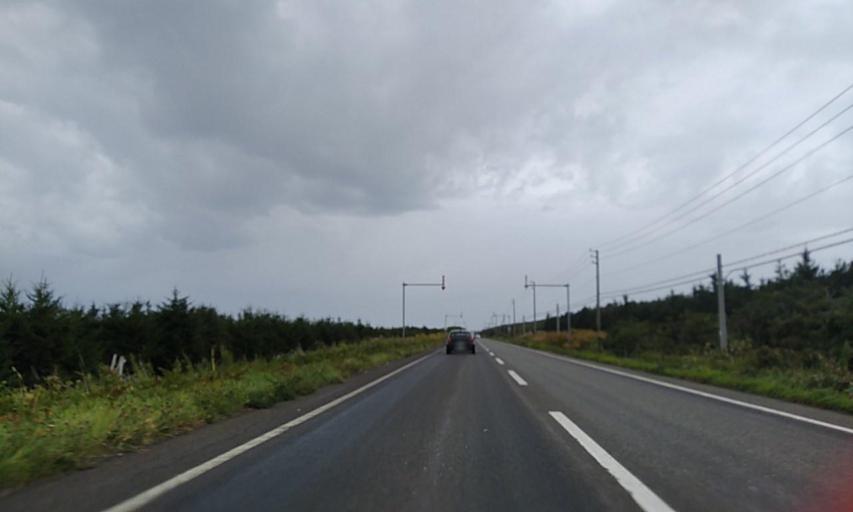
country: JP
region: Hokkaido
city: Nayoro
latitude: 44.9118
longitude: 142.5927
